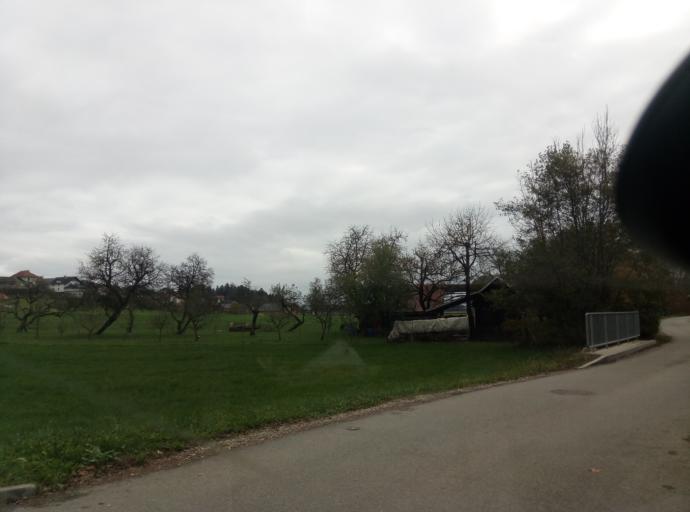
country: SI
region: Preddvor
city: Preddvor
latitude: 46.2782
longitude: 14.4344
